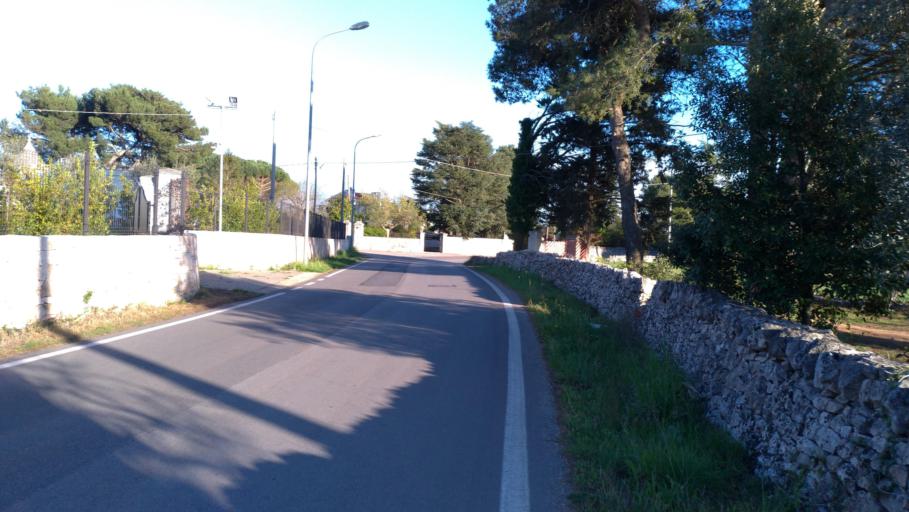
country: IT
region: Apulia
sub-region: Provincia di Taranto
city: Martina Franca
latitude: 40.6857
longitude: 17.3348
